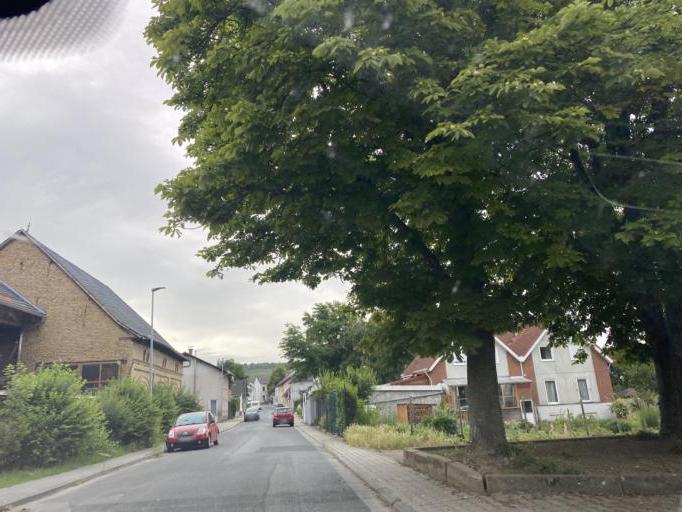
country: DE
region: Rheinland-Pfalz
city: Sprendlingen
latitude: 49.8575
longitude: 7.9865
